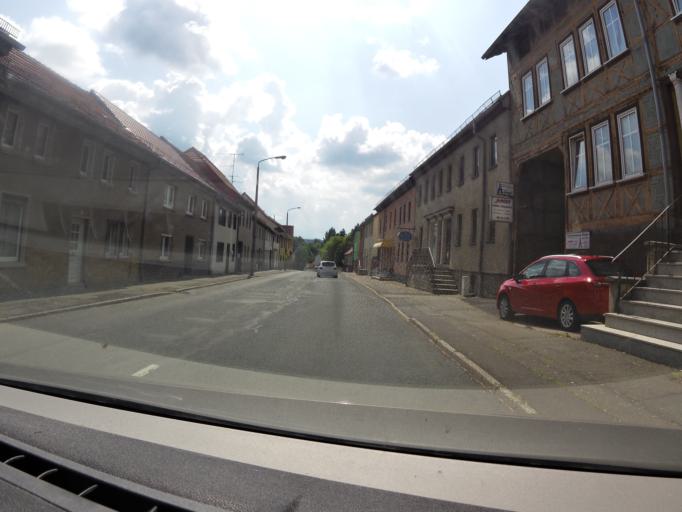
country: DE
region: Thuringia
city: Plaue
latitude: 50.7784
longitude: 10.8973
